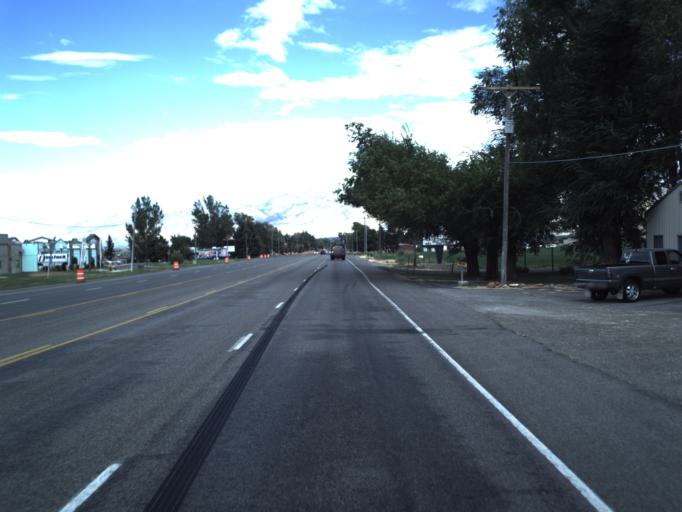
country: US
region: Utah
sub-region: Cache County
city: Nibley
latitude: 41.6819
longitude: -111.8765
